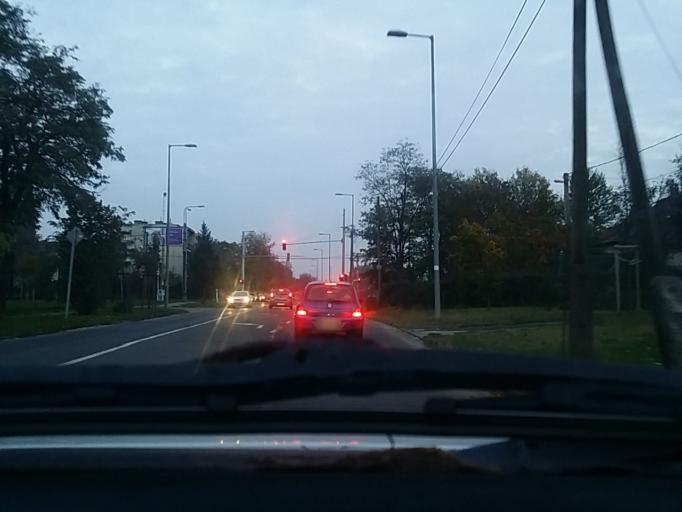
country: HU
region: Budapest
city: Budapest XIV. keruelet
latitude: 47.5255
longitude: 19.1242
